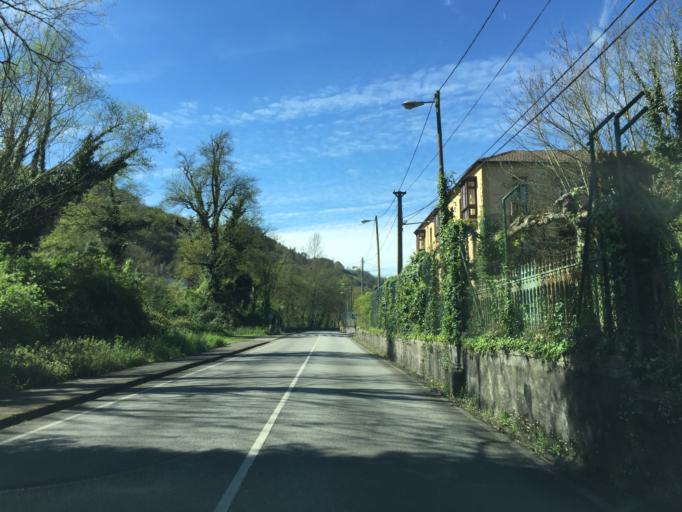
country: ES
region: Asturias
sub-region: Province of Asturias
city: Castandiello
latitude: 43.3477
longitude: -5.9704
